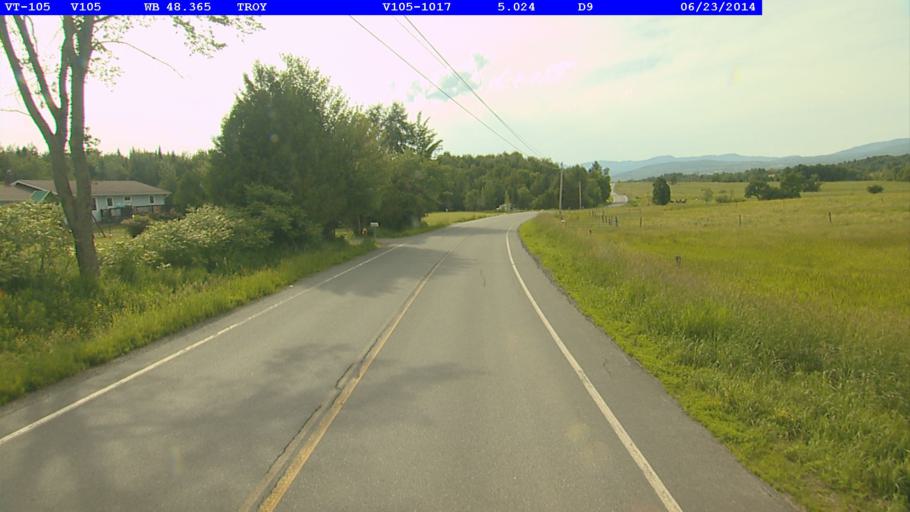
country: US
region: Vermont
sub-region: Orleans County
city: Newport
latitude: 44.9844
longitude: -72.3601
